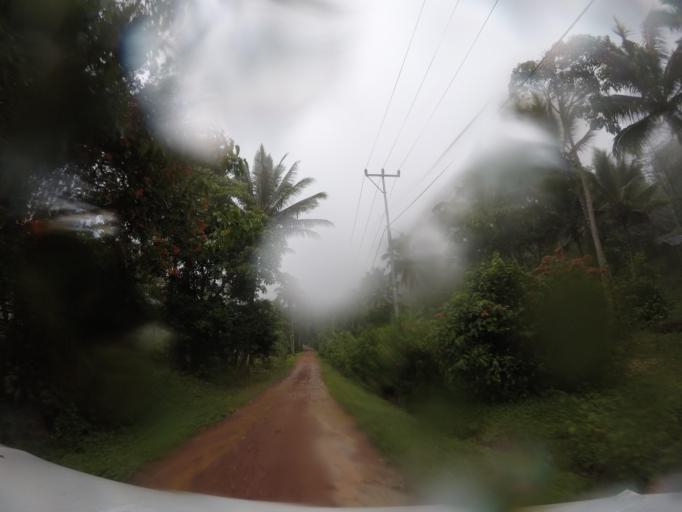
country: TL
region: Baucau
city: Venilale
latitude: -8.6334
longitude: 126.4232
